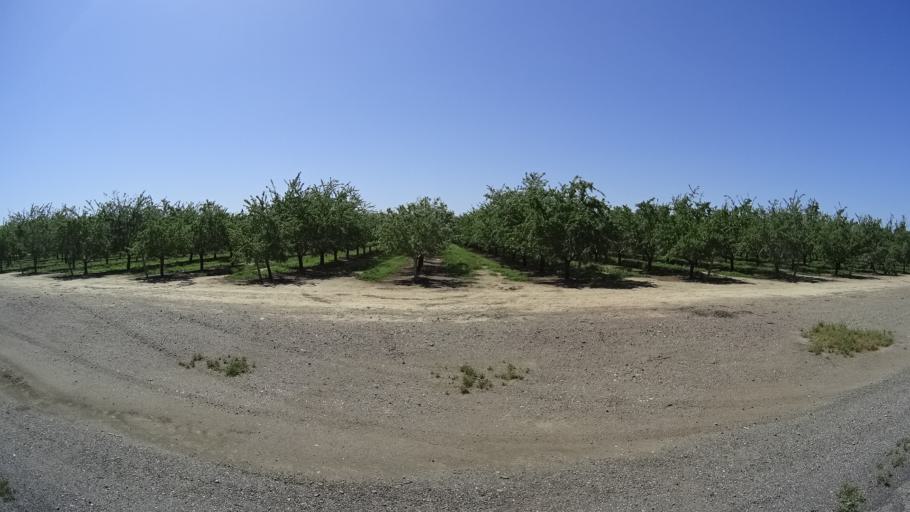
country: US
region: California
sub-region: Glenn County
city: Orland
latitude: 39.6961
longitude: -122.1347
